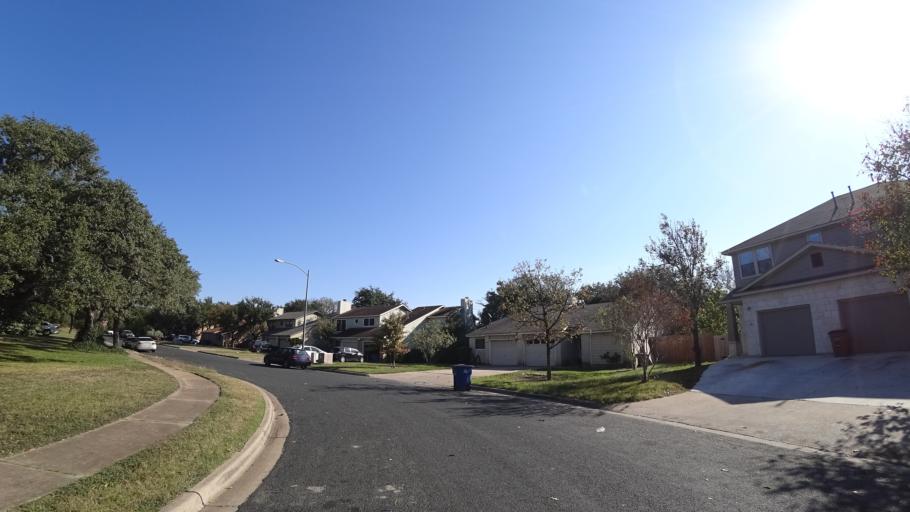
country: US
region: Texas
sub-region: Travis County
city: Barton Creek
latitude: 30.2297
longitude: -97.8443
